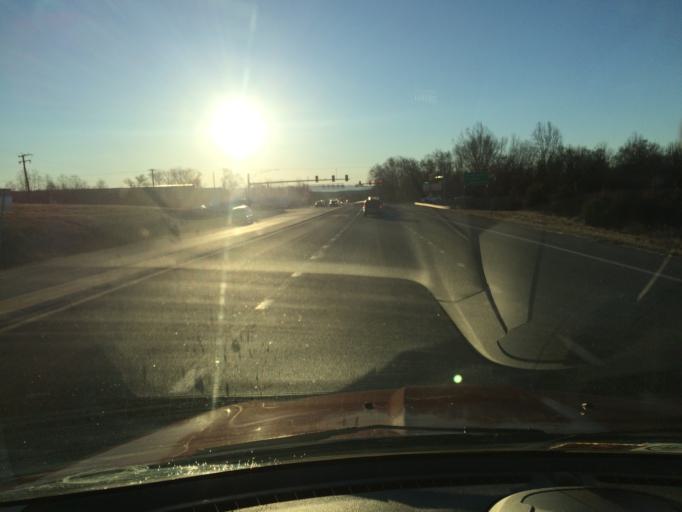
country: US
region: Virginia
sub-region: Augusta County
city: Verona
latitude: 38.1821
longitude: -79.0335
